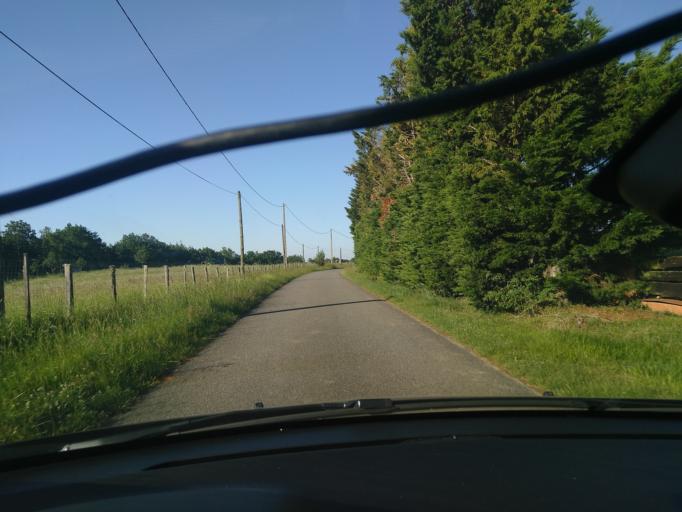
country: FR
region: Midi-Pyrenees
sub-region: Departement du Tarn-et-Garonne
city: Beaumont-de-Lomagne
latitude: 43.7880
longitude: 1.0072
